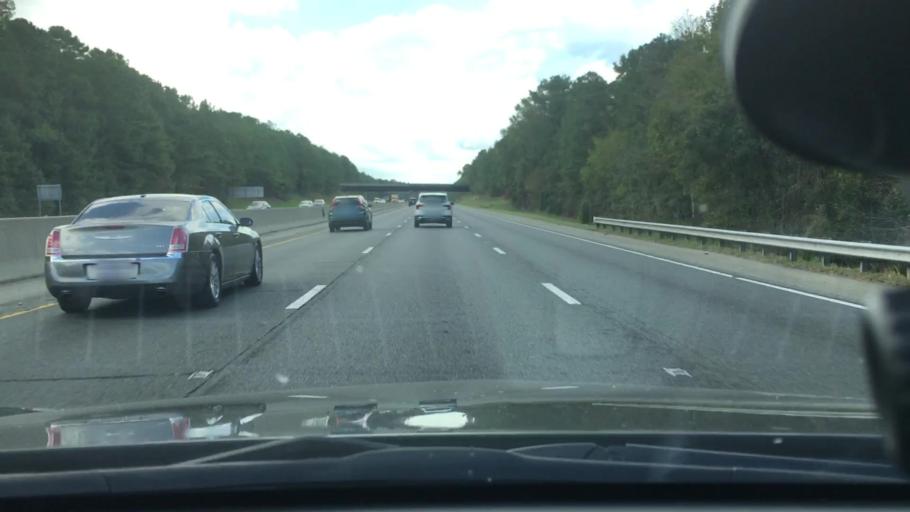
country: US
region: North Carolina
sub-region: Orange County
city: Chapel Hill
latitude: 35.9364
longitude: -78.9904
